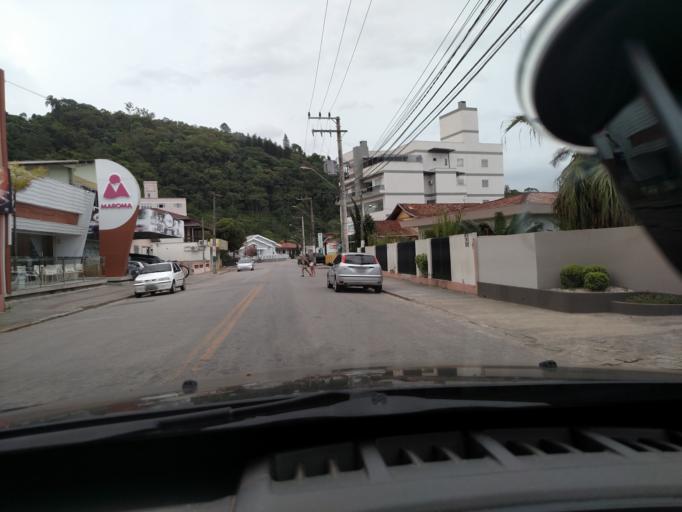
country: BR
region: Santa Catarina
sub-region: Brusque
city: Brusque
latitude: -27.0822
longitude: -48.9168
